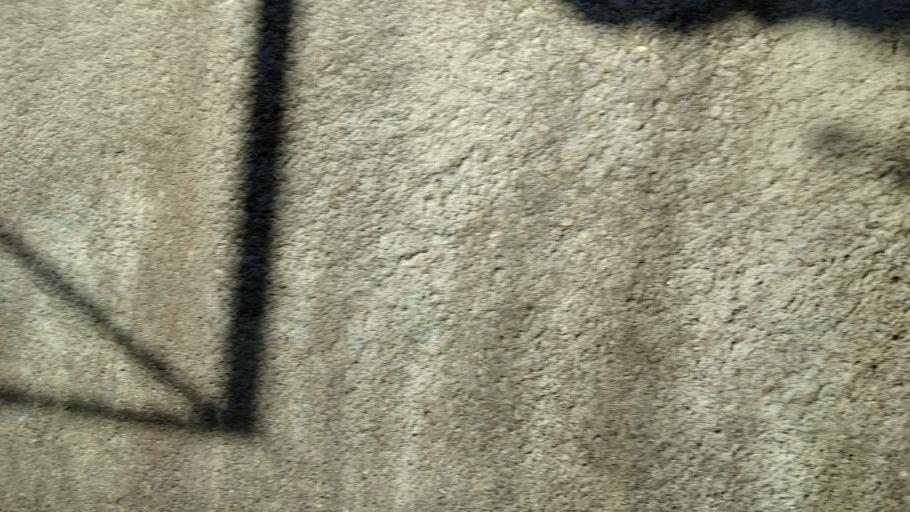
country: AL
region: Shkoder
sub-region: Rrethi i Shkodres
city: Shkoder
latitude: 42.0617
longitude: 19.5164
